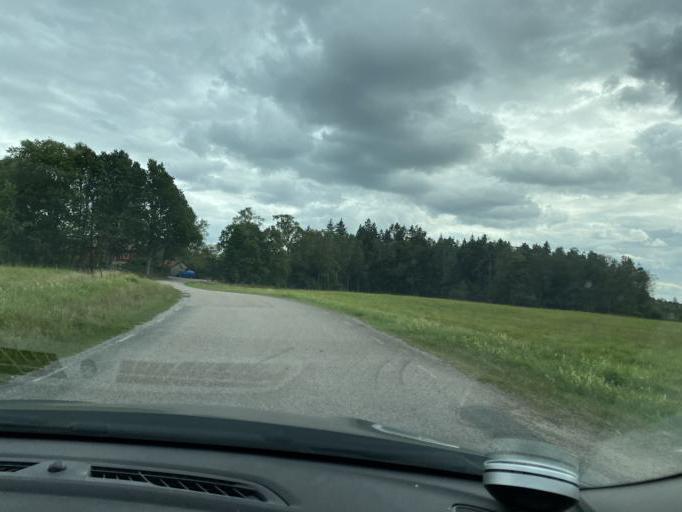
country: SE
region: Kronoberg
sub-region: Markaryds Kommun
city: Markaryd
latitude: 56.4743
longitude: 13.5652
